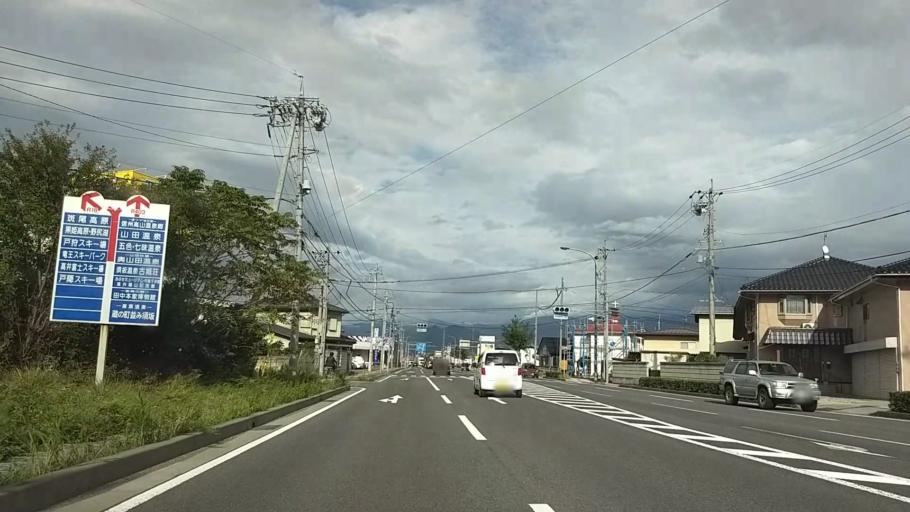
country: JP
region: Nagano
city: Suzaka
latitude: 36.6607
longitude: 138.2573
